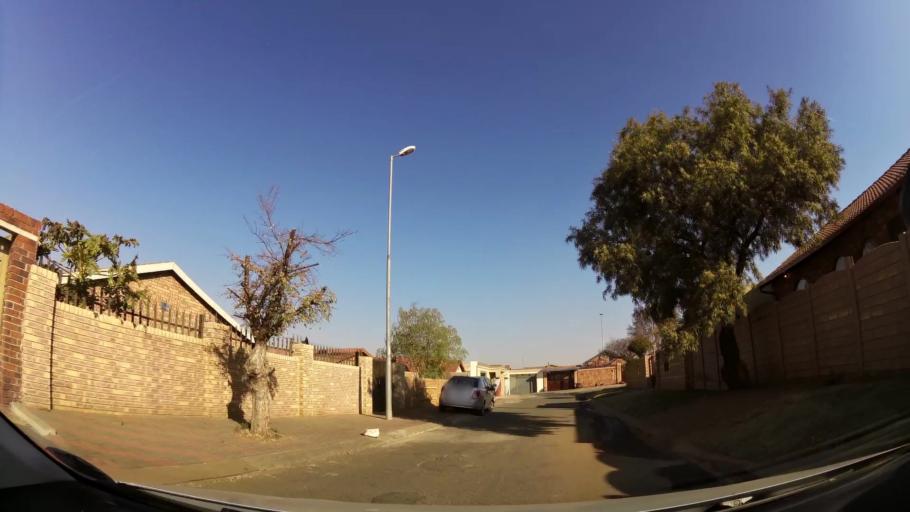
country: ZA
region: Gauteng
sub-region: City of Johannesburg Metropolitan Municipality
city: Soweto
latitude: -26.2681
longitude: 27.8788
